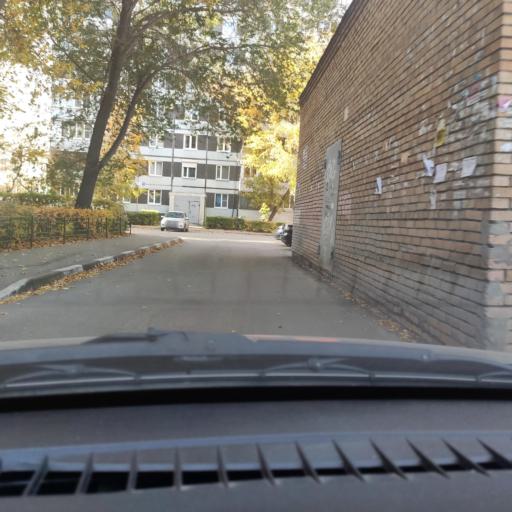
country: RU
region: Samara
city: Tol'yatti
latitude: 53.5198
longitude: 49.3126
